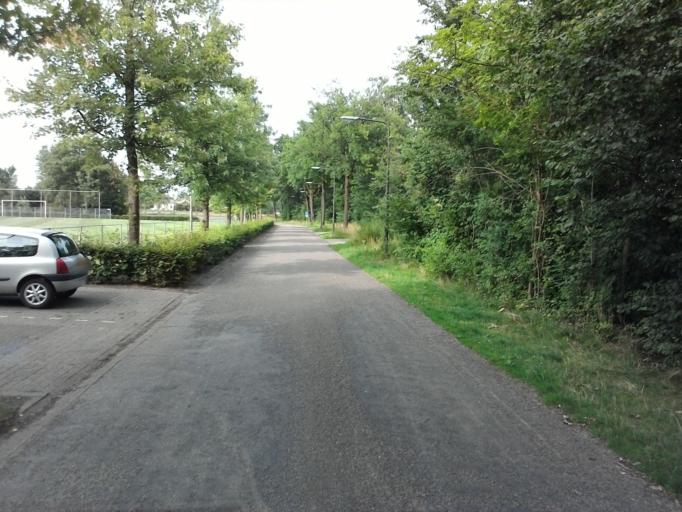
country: NL
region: North Brabant
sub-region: Gemeente Sint-Oedenrode
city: Sint-Oedenrode
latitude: 51.5659
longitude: 5.4571
